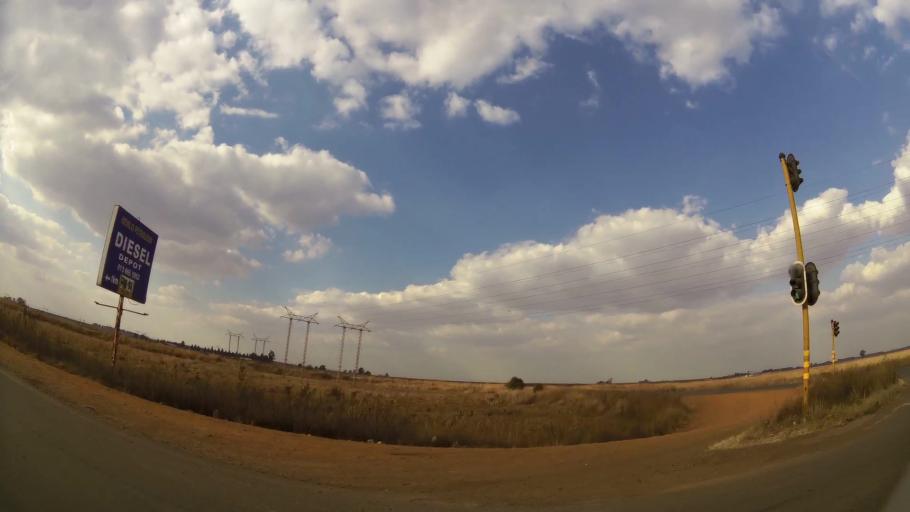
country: ZA
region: Mpumalanga
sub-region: Nkangala District Municipality
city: Delmas
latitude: -26.1541
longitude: 28.6978
